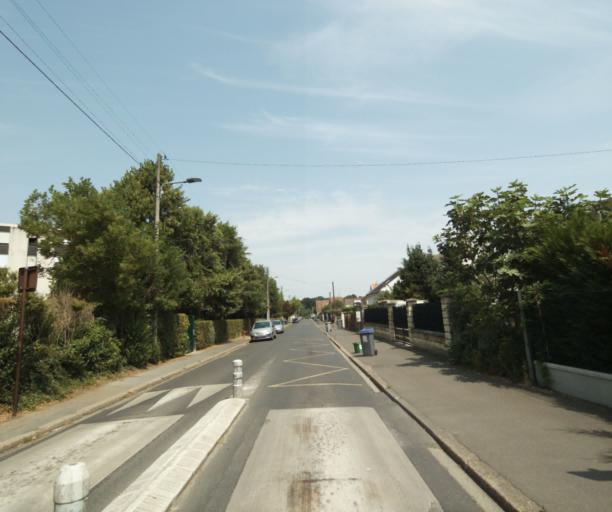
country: FR
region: Ile-de-France
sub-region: Departement des Yvelines
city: Conflans-Sainte-Honorine
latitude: 48.9976
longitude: 2.1127
